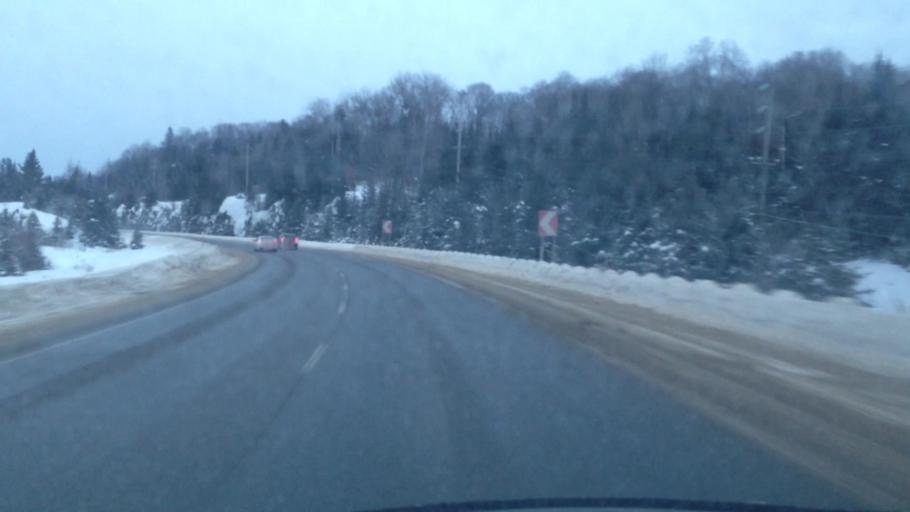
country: CA
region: Quebec
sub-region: Laurentides
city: Mont-Tremblant
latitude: 46.1088
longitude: -74.5115
